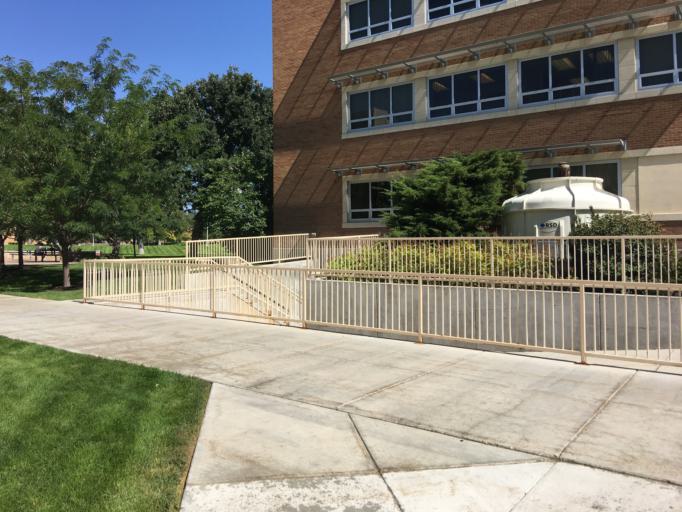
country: US
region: Idaho
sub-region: Bannock County
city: Pocatello
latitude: 42.8599
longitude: -112.4342
